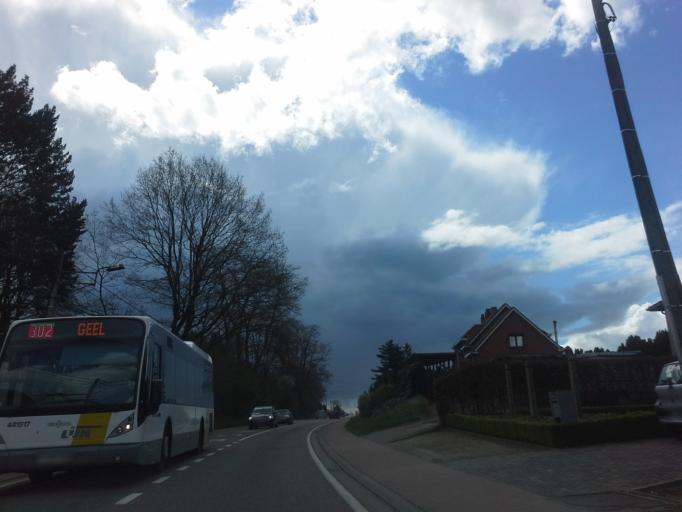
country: BE
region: Flanders
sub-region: Provincie Antwerpen
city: Meerhout
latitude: 51.1202
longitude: 5.0496
